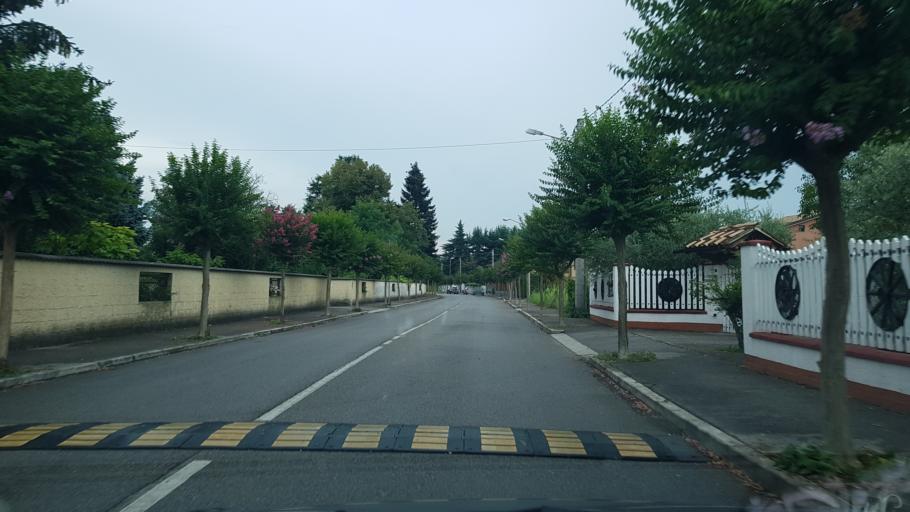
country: IT
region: Friuli Venezia Giulia
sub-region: Provincia di Gorizia
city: San Lorenzo Isontino
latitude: 45.9308
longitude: 13.5204
